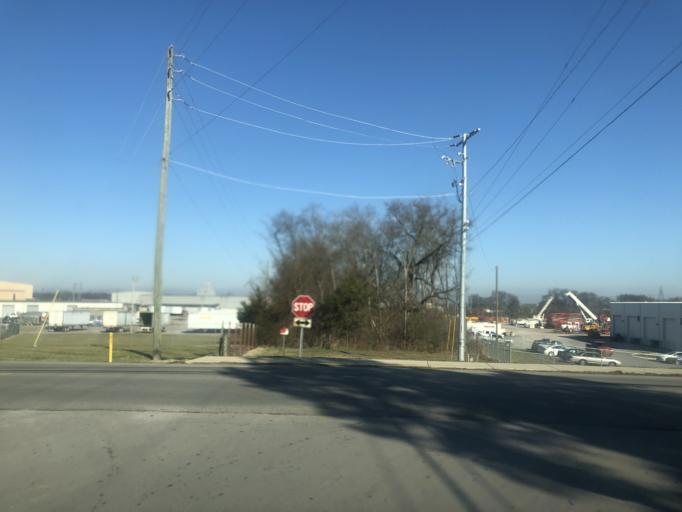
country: US
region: Tennessee
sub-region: Rutherford County
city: La Vergne
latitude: 36.0158
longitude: -86.5818
